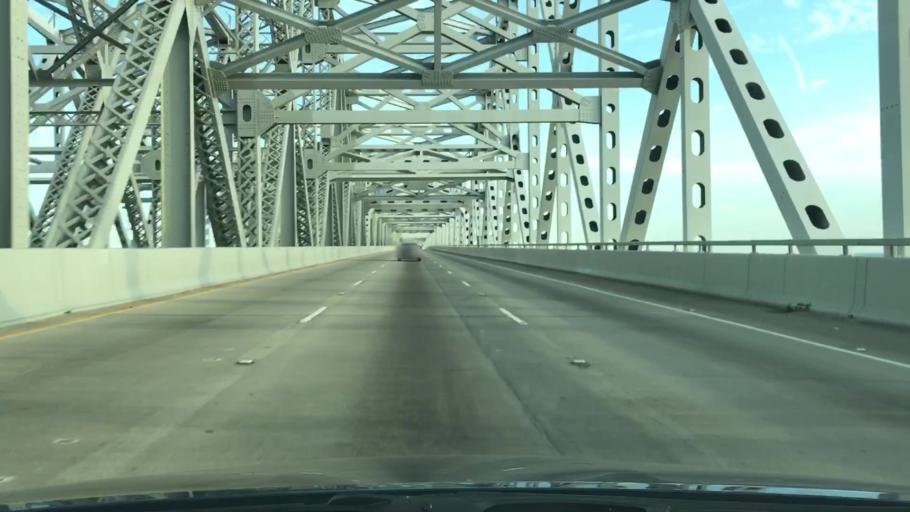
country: US
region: Louisiana
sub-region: Jefferson Parish
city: Bridge City
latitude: 29.9457
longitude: -90.1709
